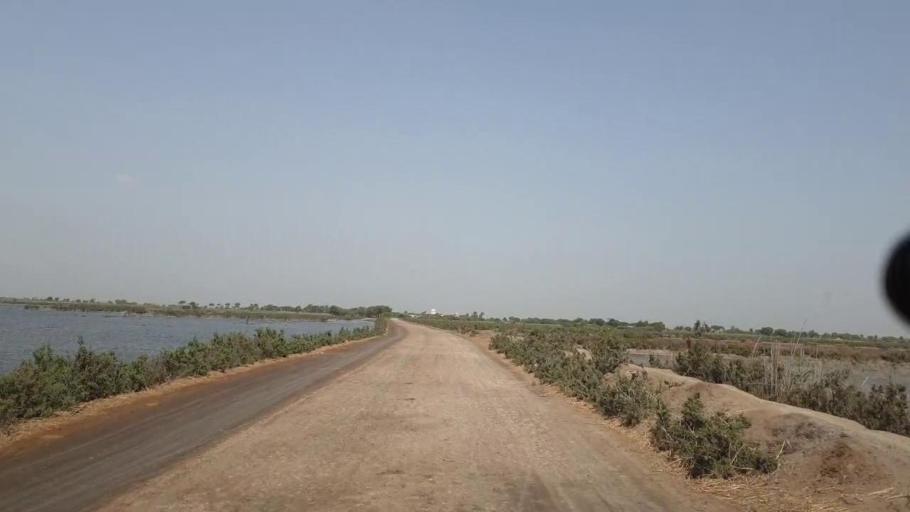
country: PK
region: Sindh
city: Matli
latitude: 25.0650
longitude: 68.7073
